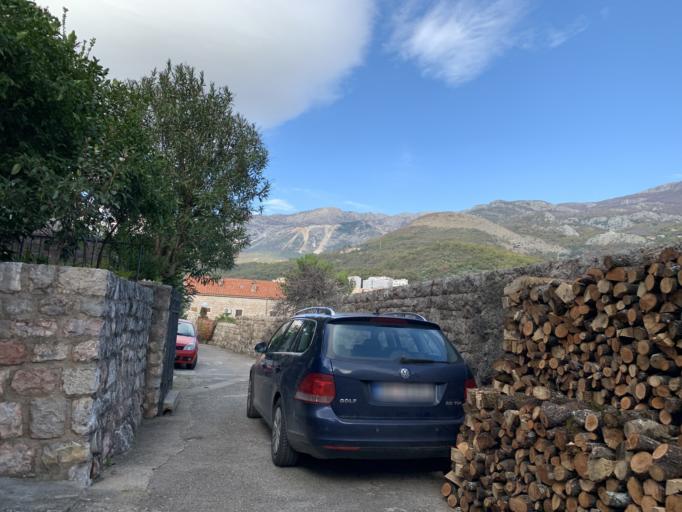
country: ME
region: Budva
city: Budva
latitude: 42.2663
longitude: 18.8917
